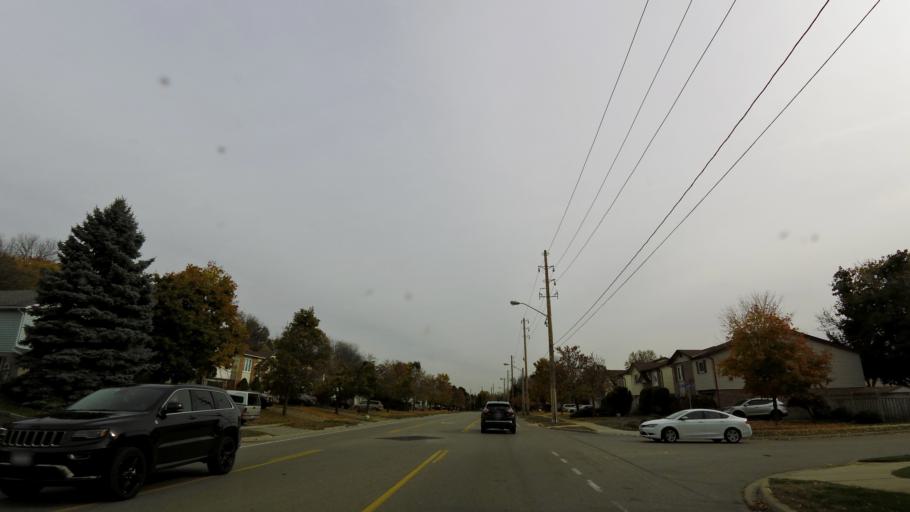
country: CA
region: Ontario
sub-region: Wellington County
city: Guelph
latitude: 43.5223
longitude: -80.2738
